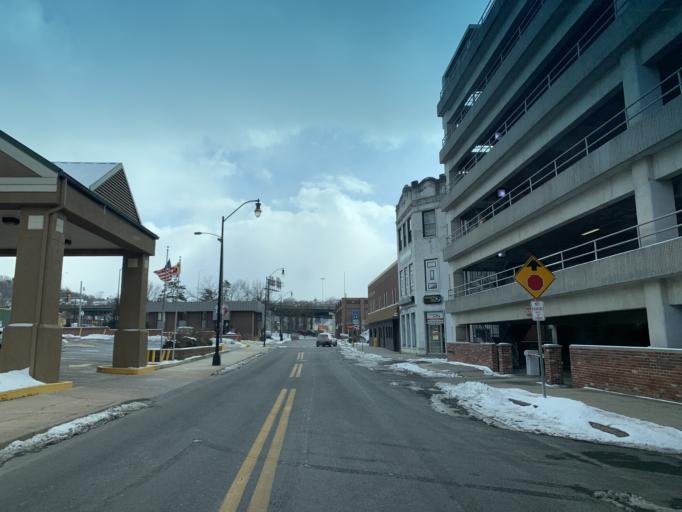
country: US
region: Maryland
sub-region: Allegany County
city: Cumberland
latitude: 39.6512
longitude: -78.7593
